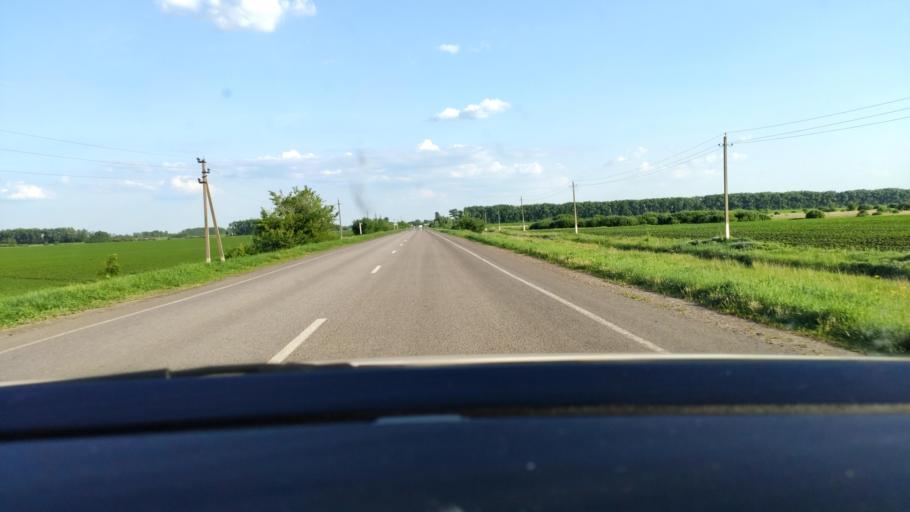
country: RU
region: Voronezj
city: Kashirskoye
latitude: 51.4760
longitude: 39.8598
